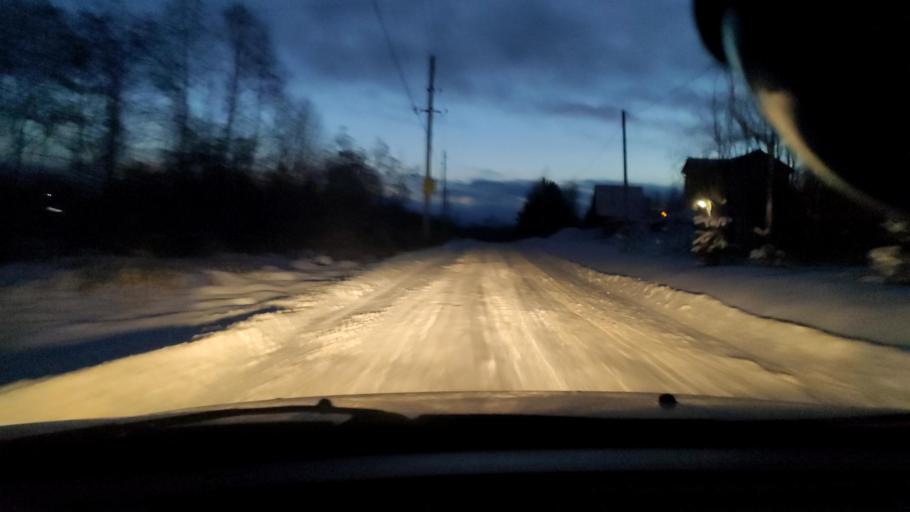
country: RU
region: Perm
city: Kultayevo
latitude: 57.9244
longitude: 55.8741
